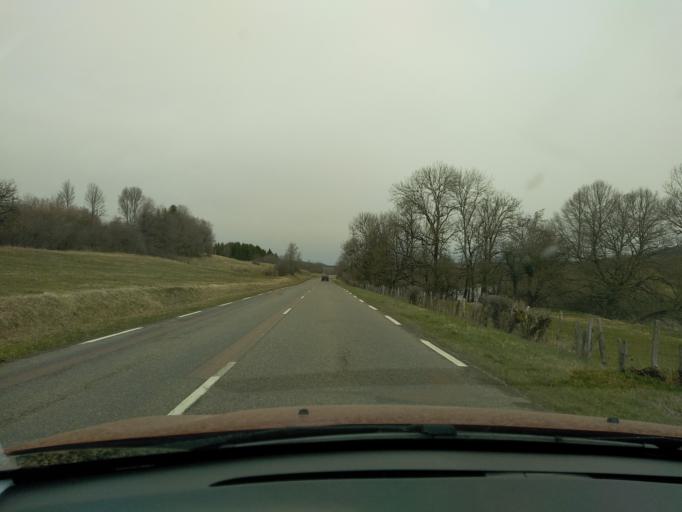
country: FR
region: Franche-Comte
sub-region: Departement du Jura
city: Champagnole
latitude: 46.7320
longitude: 5.7857
